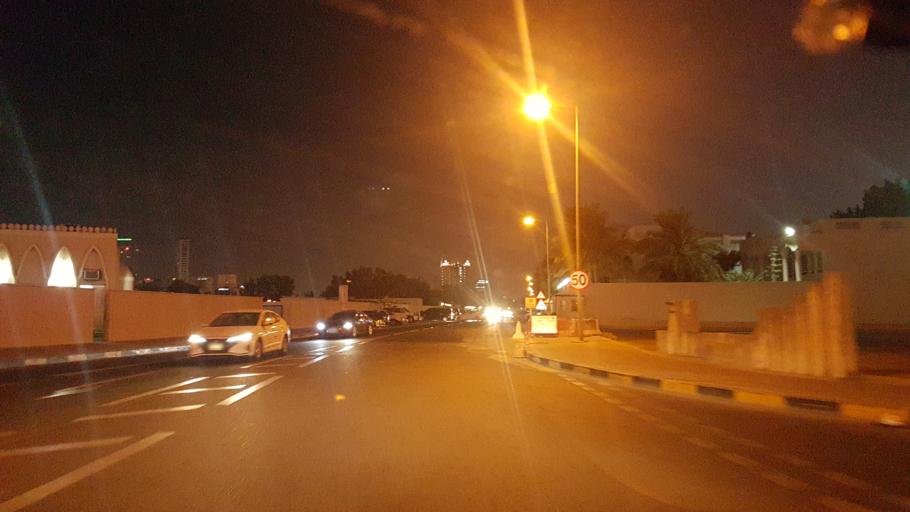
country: BH
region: Manama
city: Manama
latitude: 26.2242
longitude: 50.5951
